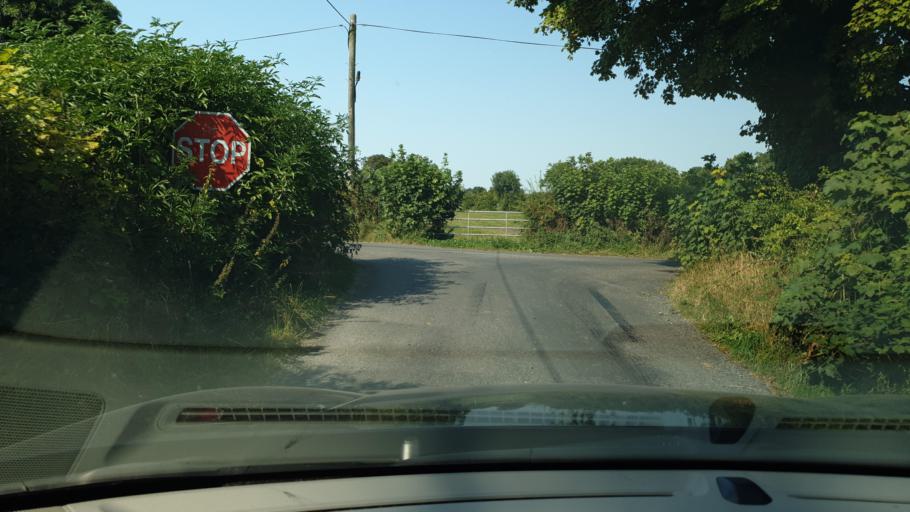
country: IE
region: Leinster
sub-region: An Mhi
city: Athboy
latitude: 53.6204
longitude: -6.9917
